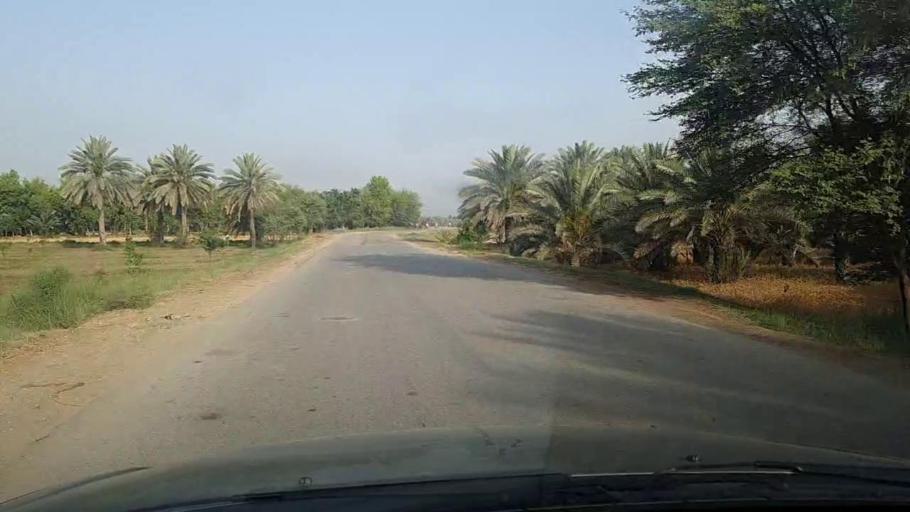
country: PK
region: Sindh
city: Pir jo Goth
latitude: 27.5621
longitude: 68.6600
